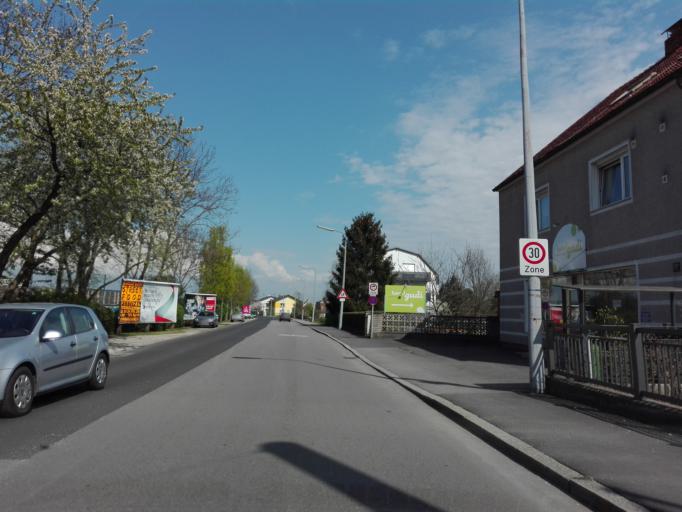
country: AT
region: Upper Austria
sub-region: Politischer Bezirk Linz-Land
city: Ansfelden
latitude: 48.2462
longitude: 14.2868
